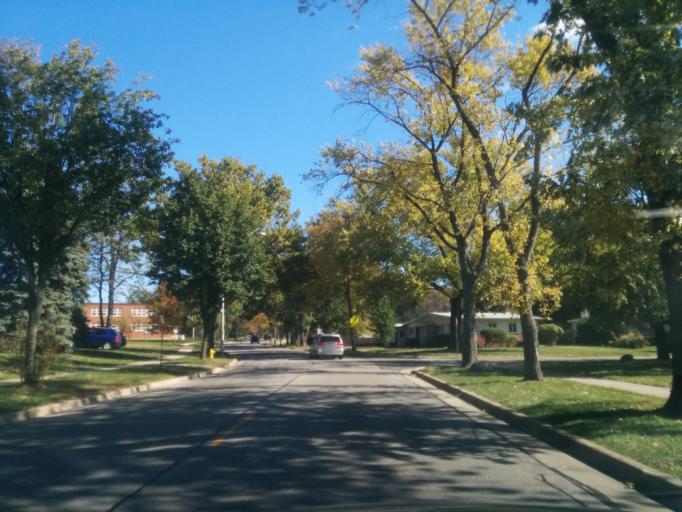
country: US
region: Illinois
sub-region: DuPage County
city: Lombard
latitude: 41.8746
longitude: -88.0240
